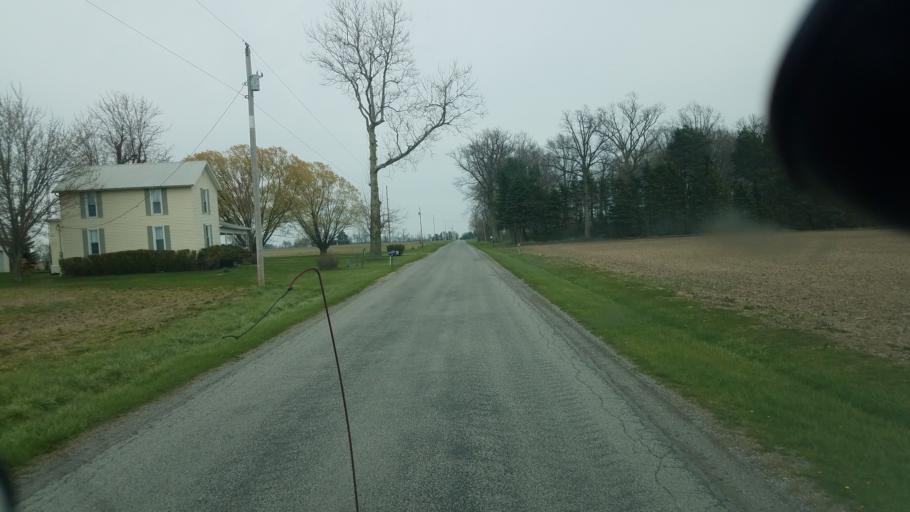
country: US
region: Ohio
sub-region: Hardin County
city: Forest
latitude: 40.8908
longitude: -83.5229
